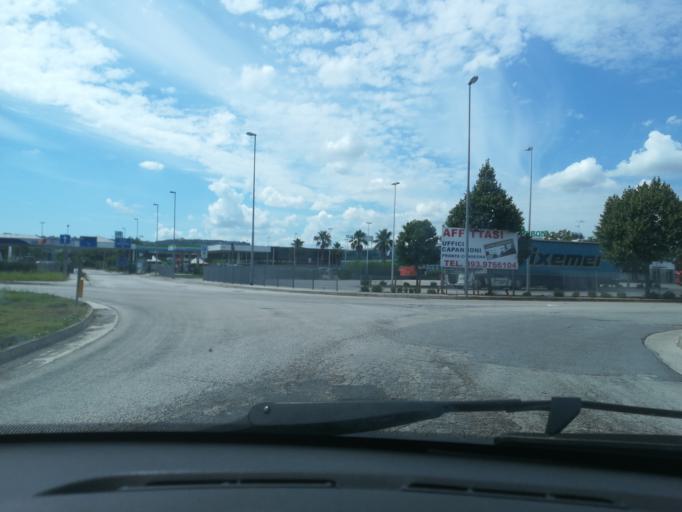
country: IT
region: The Marches
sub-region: Provincia di Macerata
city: Santa Maria Apparente
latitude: 43.2835
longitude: 13.6831
